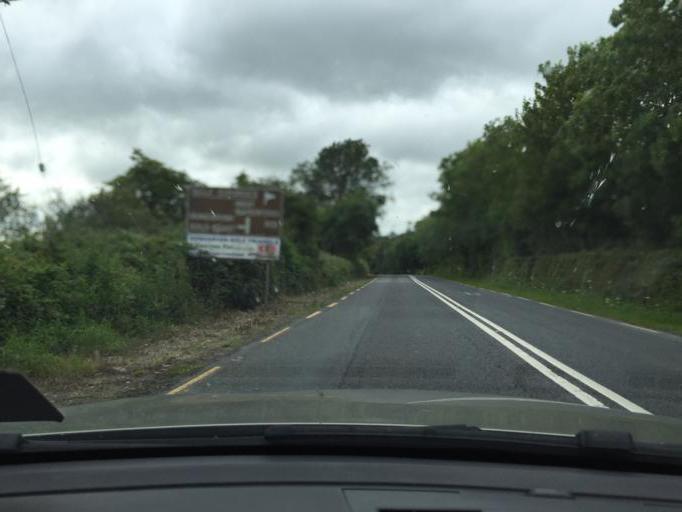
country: IE
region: Munster
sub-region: Waterford
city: Dungarvan
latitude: 52.1145
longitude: -7.5700
